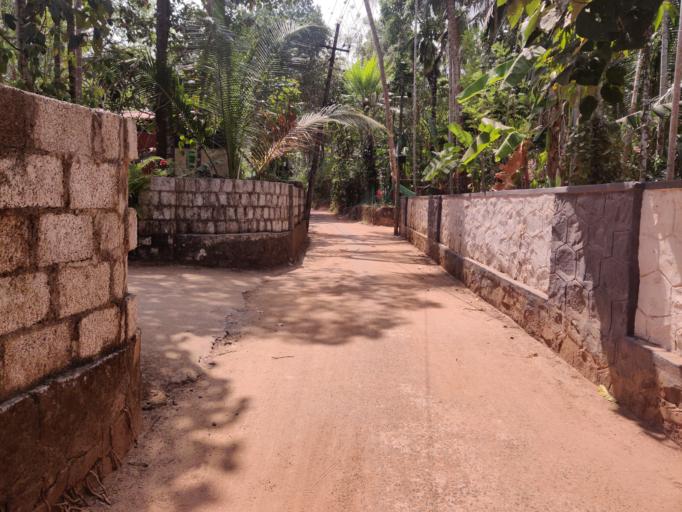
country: IN
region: Kerala
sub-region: Malappuram
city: Ponnani
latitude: 10.7307
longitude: 76.0026
